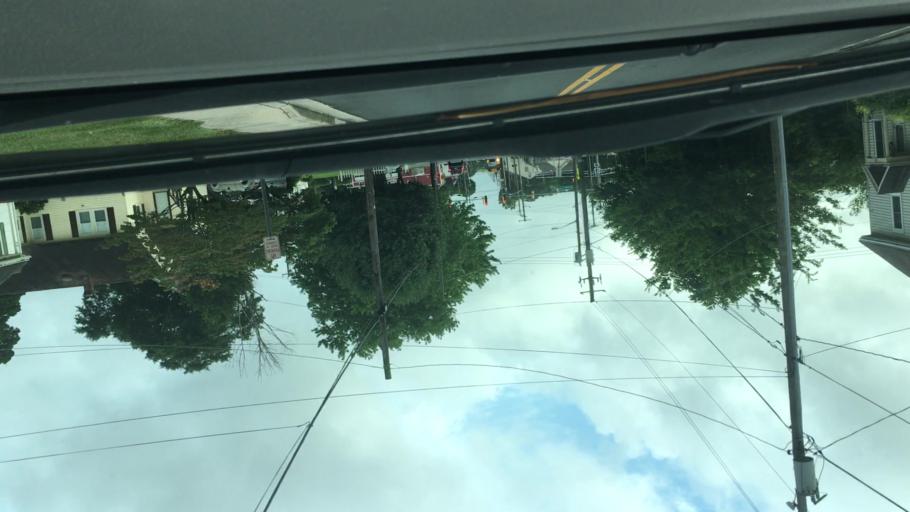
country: US
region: Maryland
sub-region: Wicomico County
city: Fruitland
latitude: 38.3232
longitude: -75.6204
